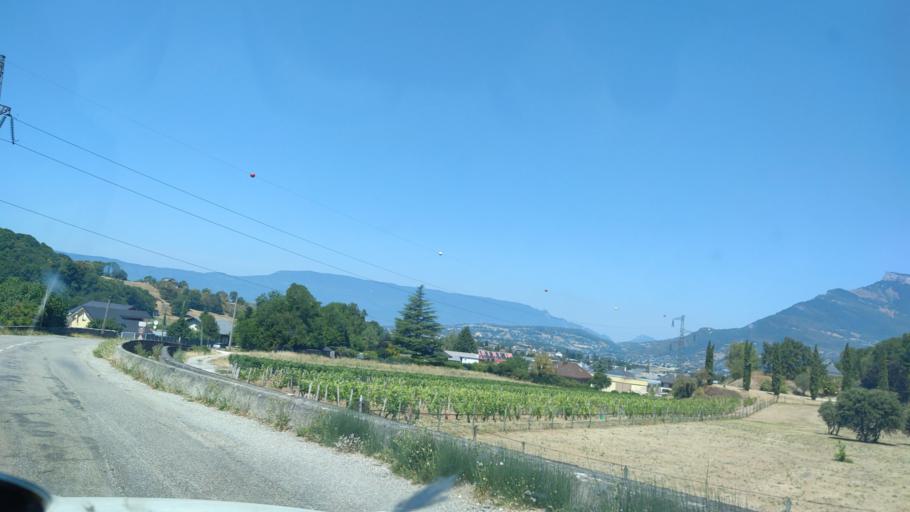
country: FR
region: Rhone-Alpes
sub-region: Departement de la Savoie
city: Challes-les-Eaux
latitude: 45.5382
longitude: 5.9946
